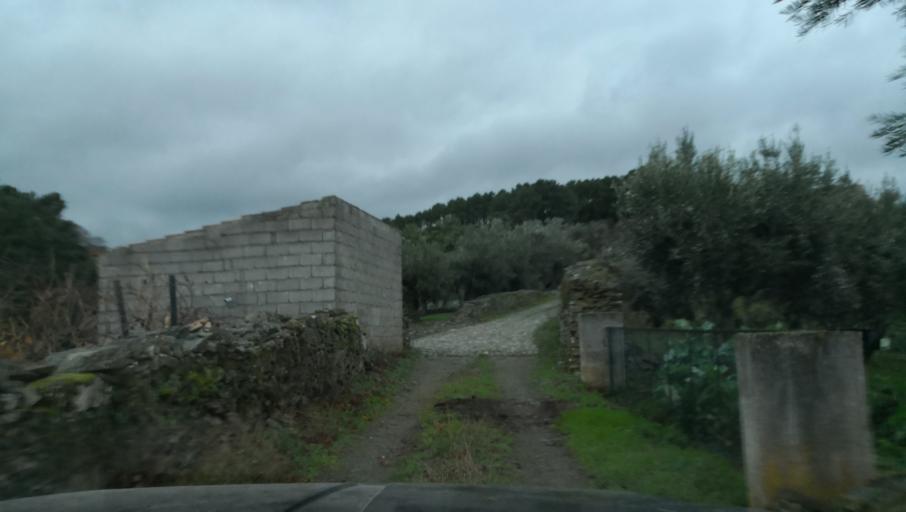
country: PT
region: Vila Real
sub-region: Vila Real
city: Vila Real
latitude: 41.2485
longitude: -7.7390
